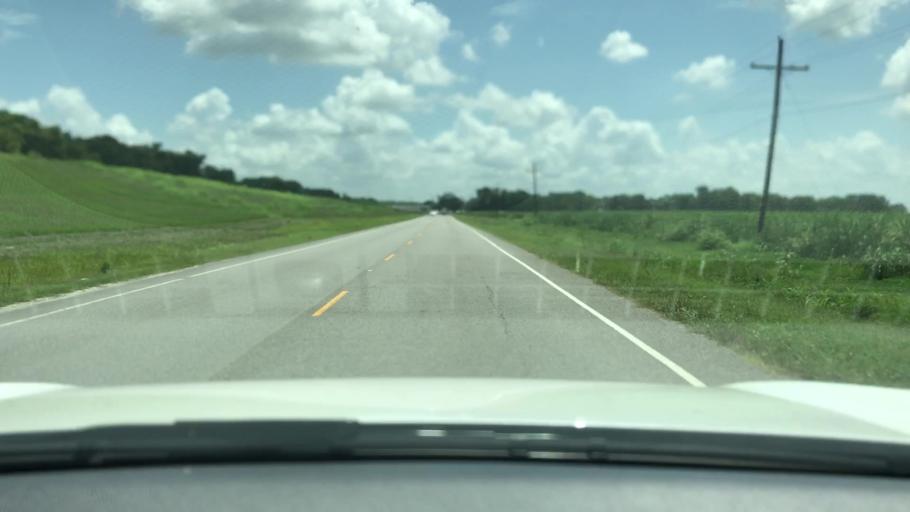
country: US
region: Louisiana
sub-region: Iberville Parish
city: Plaquemine
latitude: 30.2728
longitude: -91.1960
